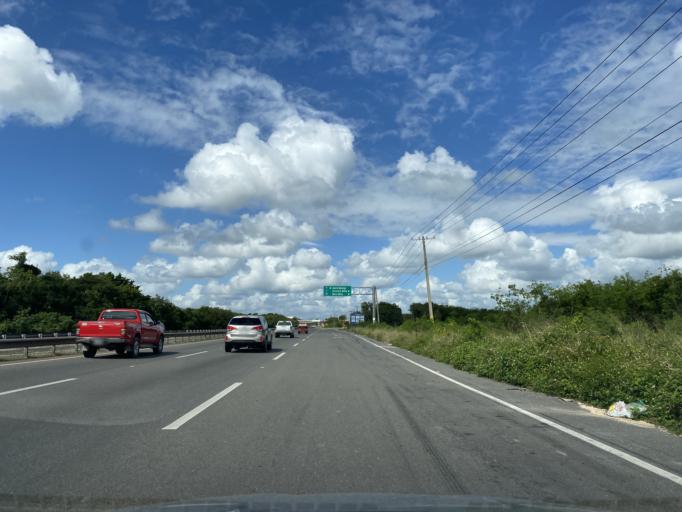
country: DO
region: Santo Domingo
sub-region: Santo Domingo
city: Boca Chica
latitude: 18.4475
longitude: -69.5912
